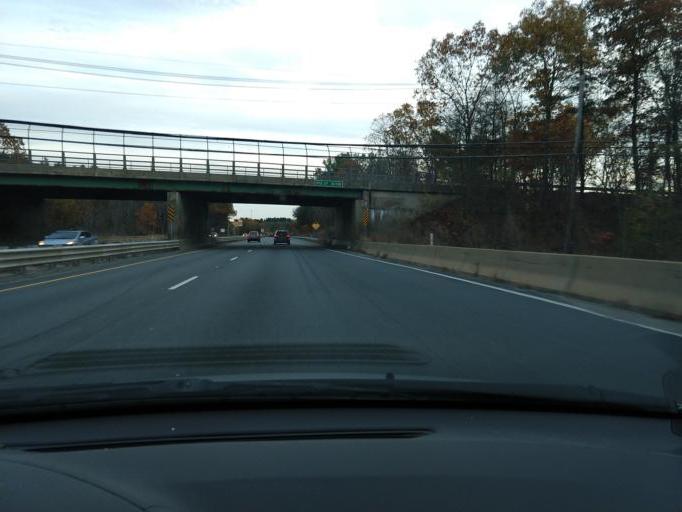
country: US
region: Massachusetts
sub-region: Middlesex County
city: Acton
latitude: 42.4783
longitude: -71.4489
